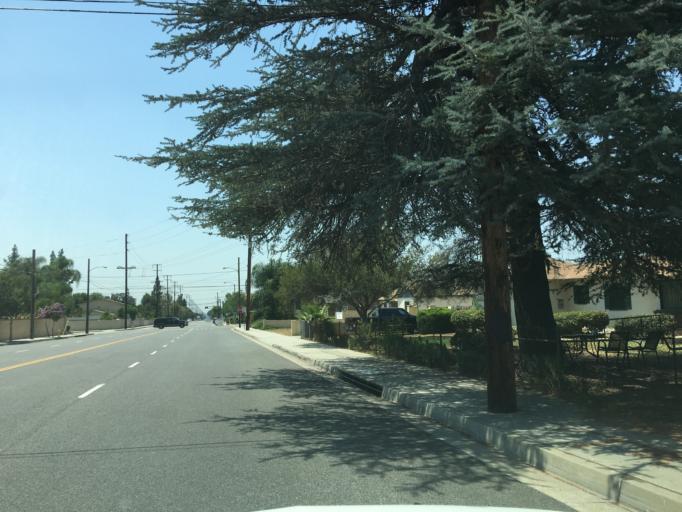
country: US
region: California
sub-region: Los Angeles County
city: Charter Oak
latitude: 34.0995
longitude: -117.8451
